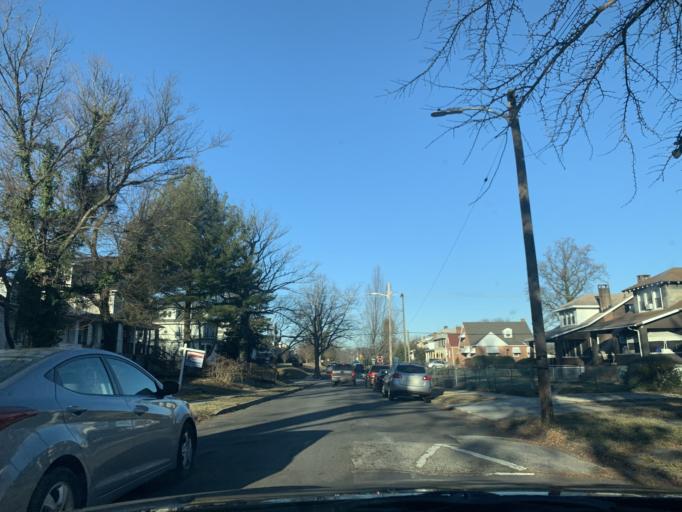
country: US
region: Maryland
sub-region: Baltimore County
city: Lochearn
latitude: 39.3252
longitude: -76.6883
